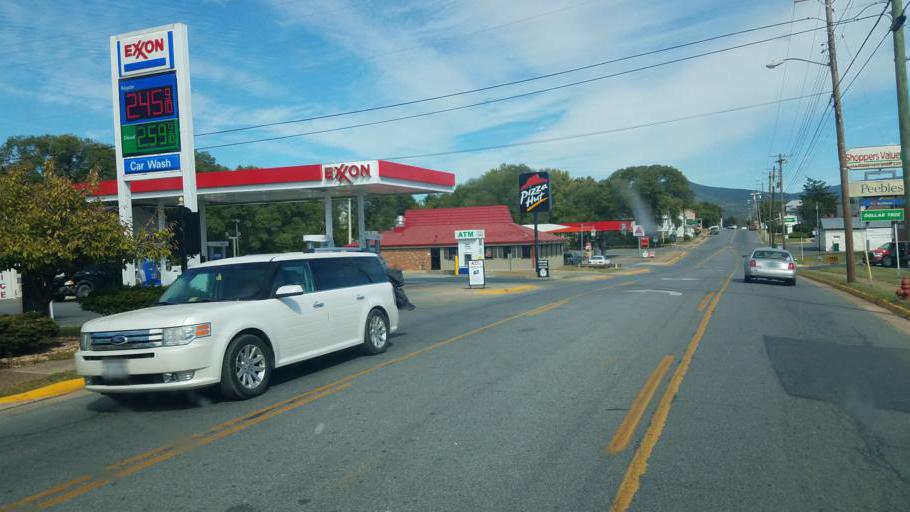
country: US
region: Virginia
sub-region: Page County
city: Luray
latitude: 38.6656
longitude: -78.4479
